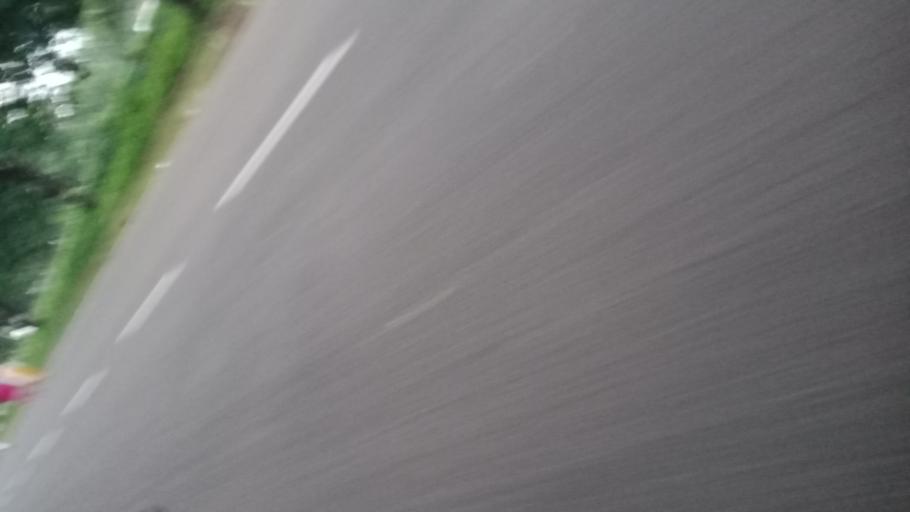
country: IN
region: Telangana
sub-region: Medak
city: Serilingampalle
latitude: 17.4944
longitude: 78.3095
